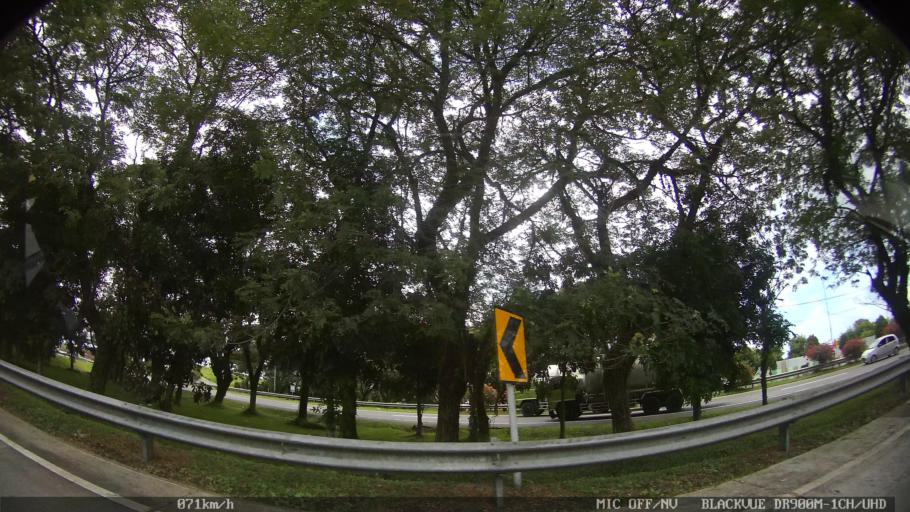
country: ID
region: North Sumatra
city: Medan
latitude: 3.6354
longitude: 98.7095
